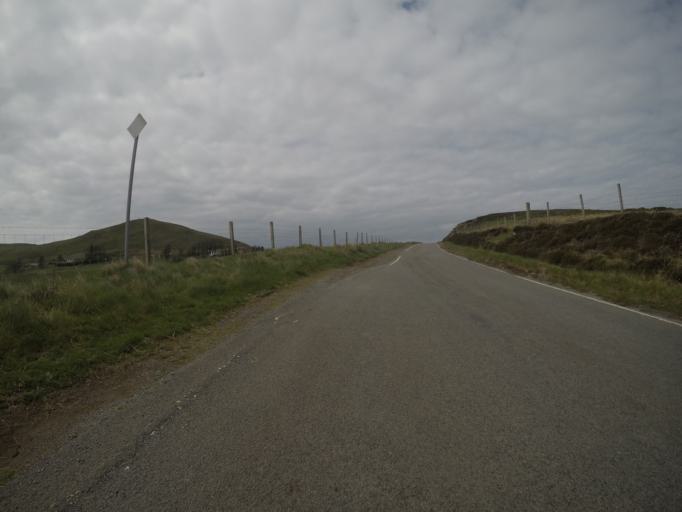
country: GB
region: Scotland
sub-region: Highland
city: Portree
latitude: 57.6822
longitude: -6.3233
